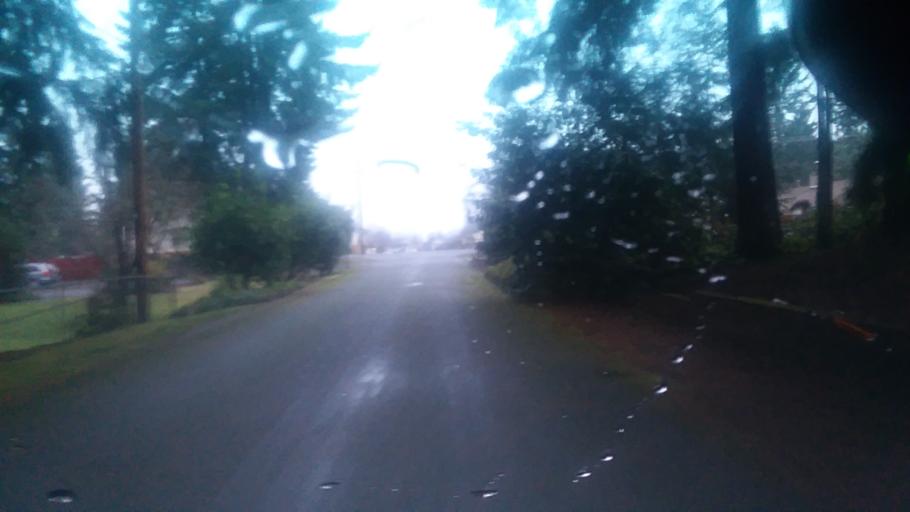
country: US
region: Washington
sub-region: Pierce County
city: South Hill
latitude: 47.1249
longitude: -122.2845
